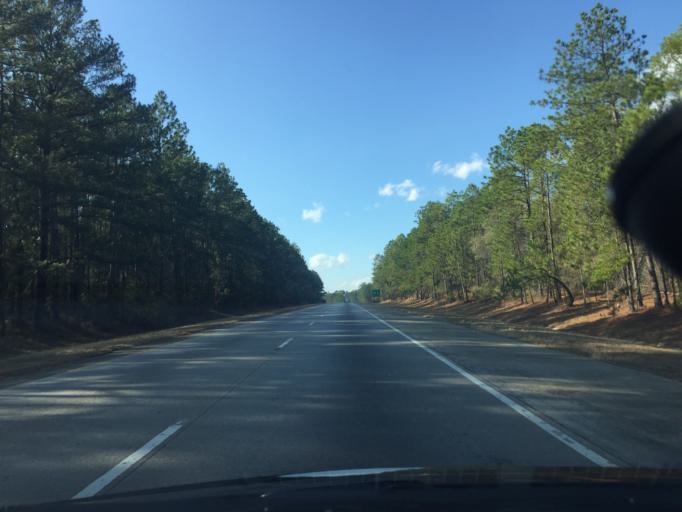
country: US
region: Georgia
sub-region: Treutlen County
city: Soperton
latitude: 32.4331
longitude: -82.4926
